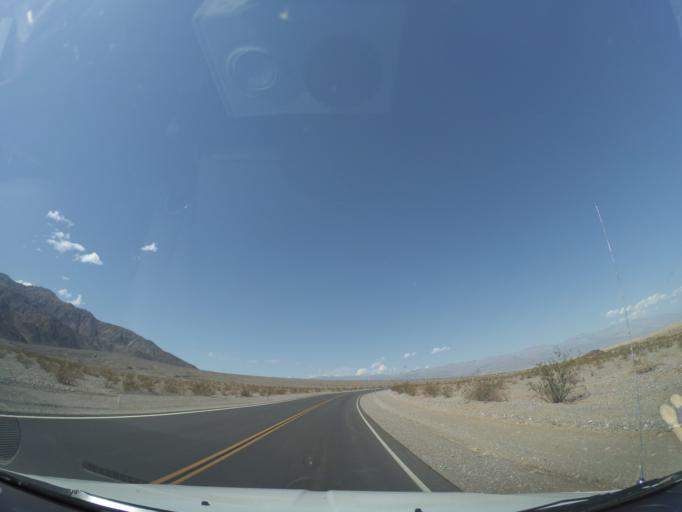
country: US
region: Nevada
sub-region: Nye County
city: Beatty
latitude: 36.6072
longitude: -117.0961
